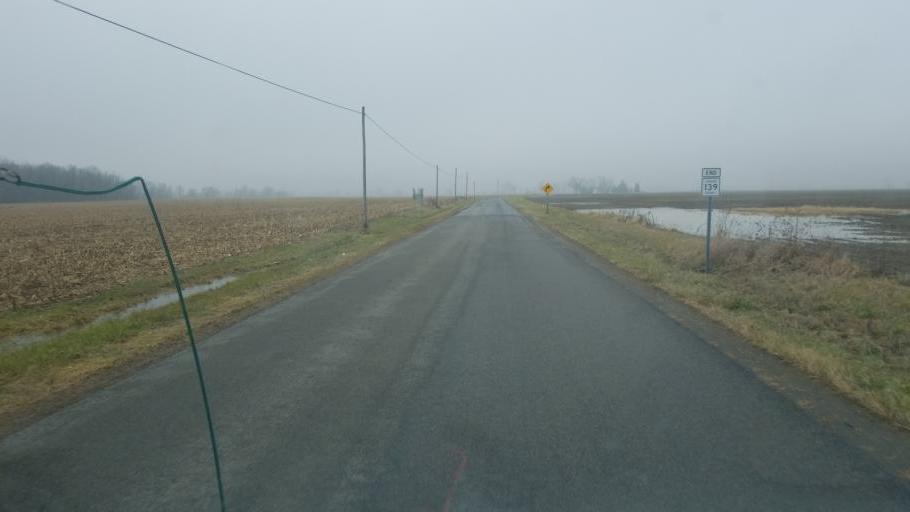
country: US
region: Ohio
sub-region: Hardin County
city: Kenton
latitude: 40.5090
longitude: -83.5214
